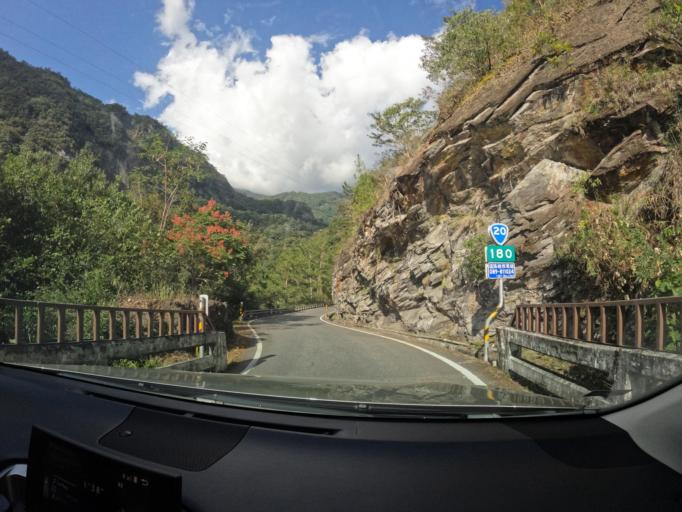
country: TW
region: Taiwan
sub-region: Taitung
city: Taitung
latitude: 23.1717
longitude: 121.0376
